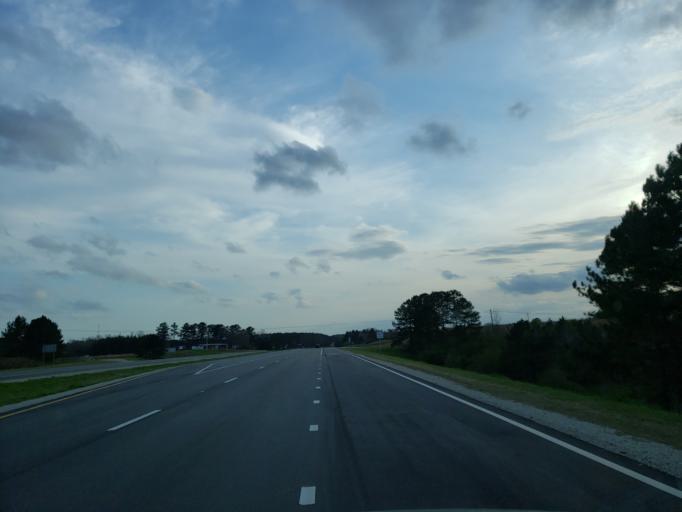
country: US
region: Mississippi
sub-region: Clarke County
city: Stonewall
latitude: 32.2154
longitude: -88.6971
